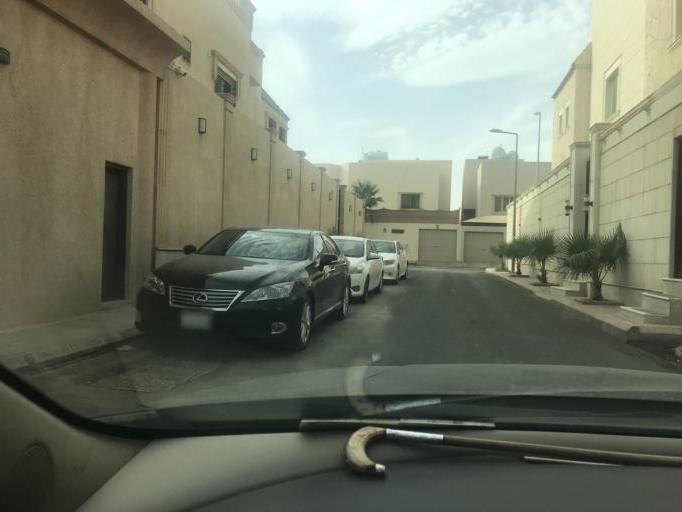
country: SA
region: Ar Riyad
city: Riyadh
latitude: 24.7977
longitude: 46.6695
